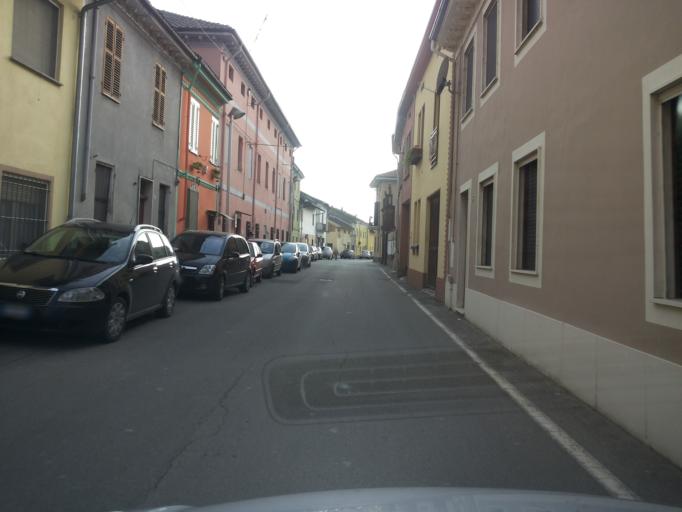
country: IT
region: Piedmont
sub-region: Provincia di Vercelli
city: Motta De Conti
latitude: 45.1935
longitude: 8.5207
